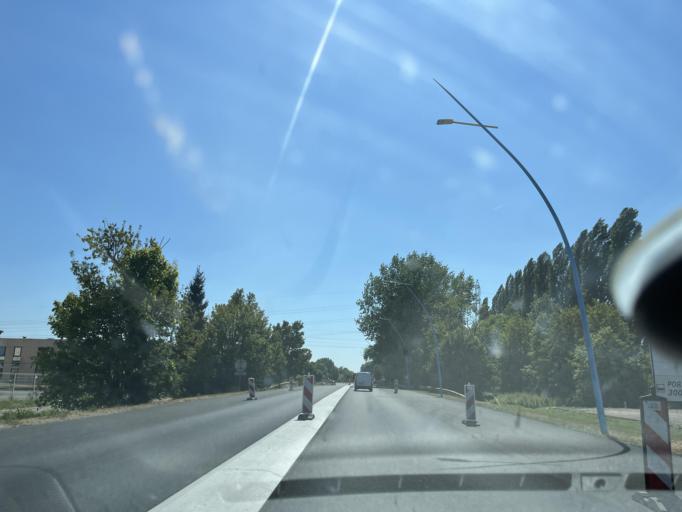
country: FR
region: Haute-Normandie
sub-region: Departement de la Seine-Maritime
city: Lillebonne
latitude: 49.4952
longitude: 0.5352
